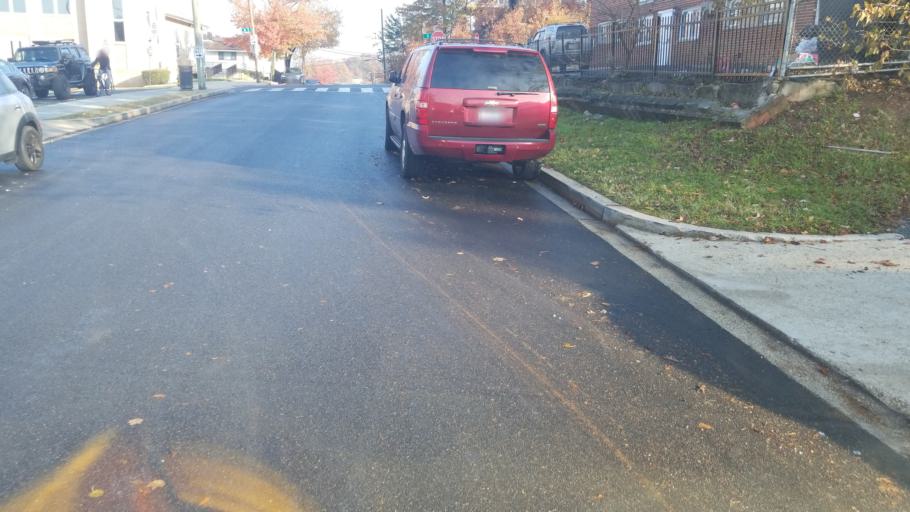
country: US
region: Maryland
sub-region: Prince George's County
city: Capitol Heights
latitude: 38.8862
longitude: -76.9305
